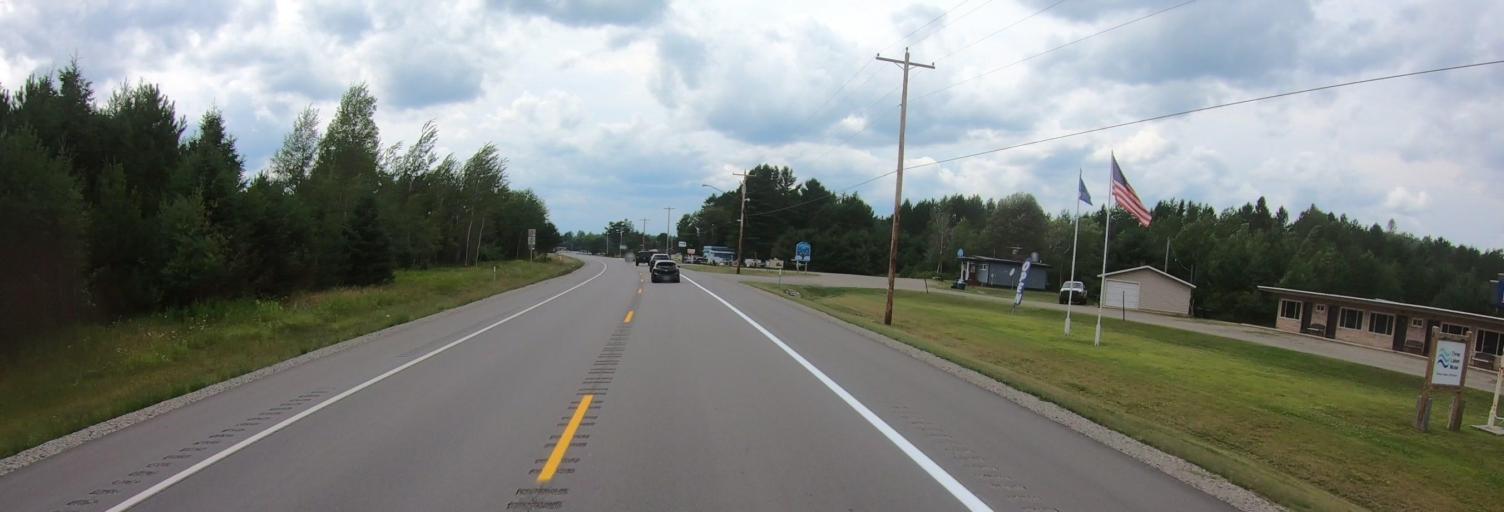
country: US
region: Michigan
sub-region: Baraga County
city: L'Anse
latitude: 46.5544
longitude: -88.2025
